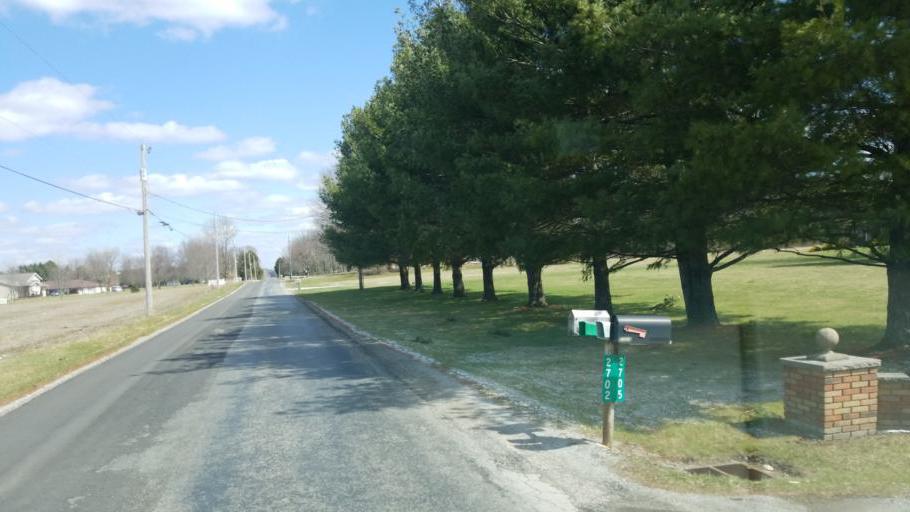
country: US
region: Ohio
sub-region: Richland County
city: Shelby
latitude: 40.8862
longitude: -82.6318
